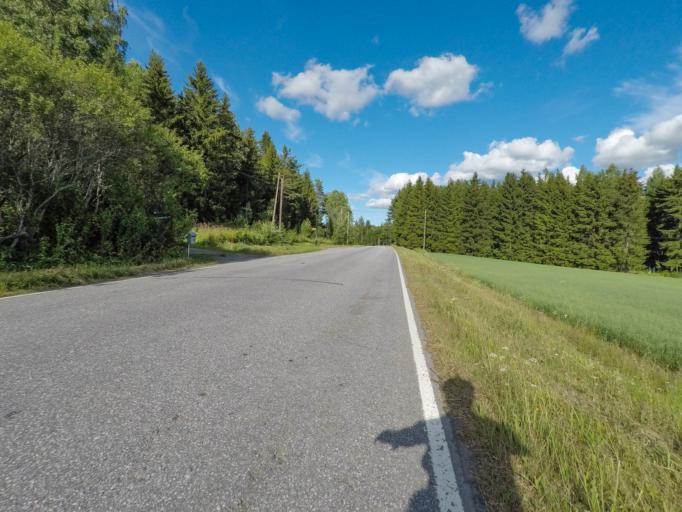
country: FI
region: South Karelia
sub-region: Imatra
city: Imatra
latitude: 61.1299
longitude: 28.7206
